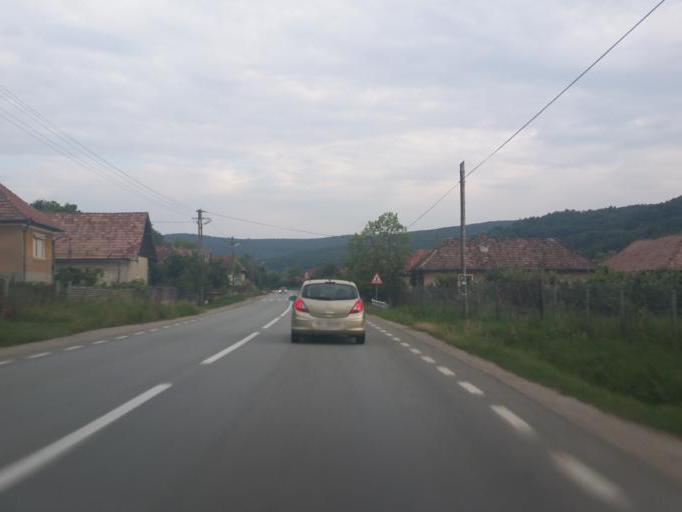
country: RO
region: Salaj
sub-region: Comuna Zimbor
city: Zimbor
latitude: 46.9863
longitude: 23.2515
